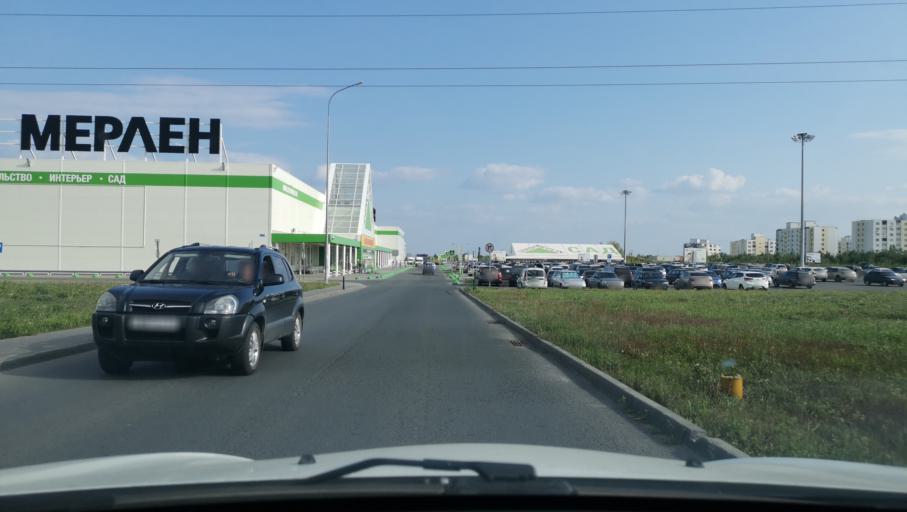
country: RU
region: Saratov
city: Engel's
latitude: 51.5907
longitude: 46.1268
